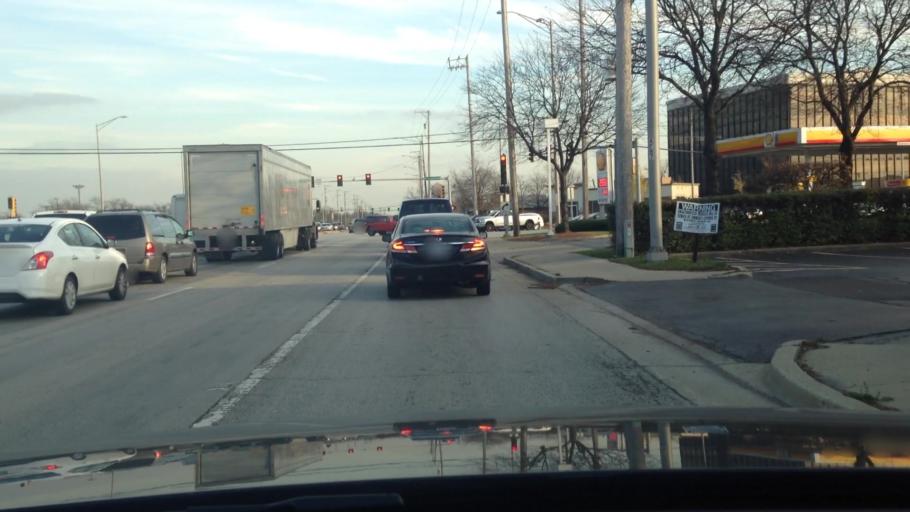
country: US
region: Illinois
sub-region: Cook County
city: Elk Grove Village
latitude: 42.0444
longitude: -87.9840
